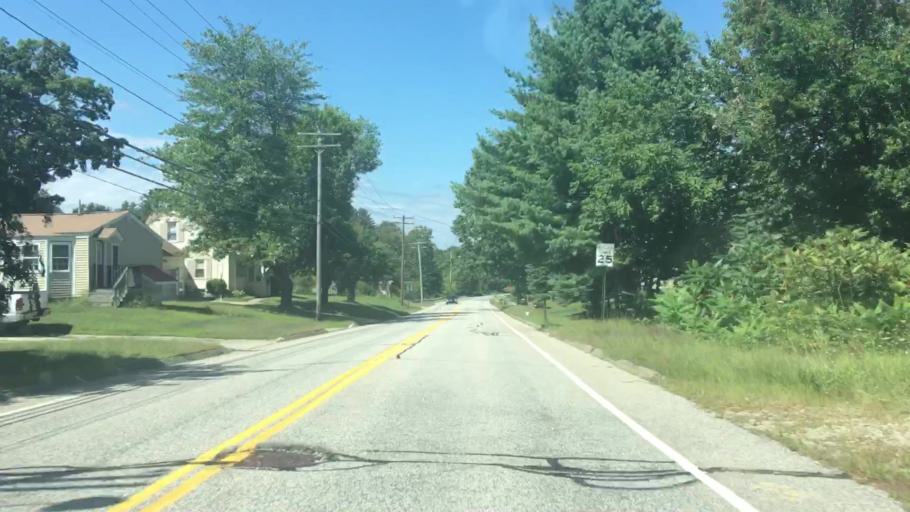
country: US
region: Maine
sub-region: Androscoggin County
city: Sabattus
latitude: 44.0893
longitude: -70.1450
